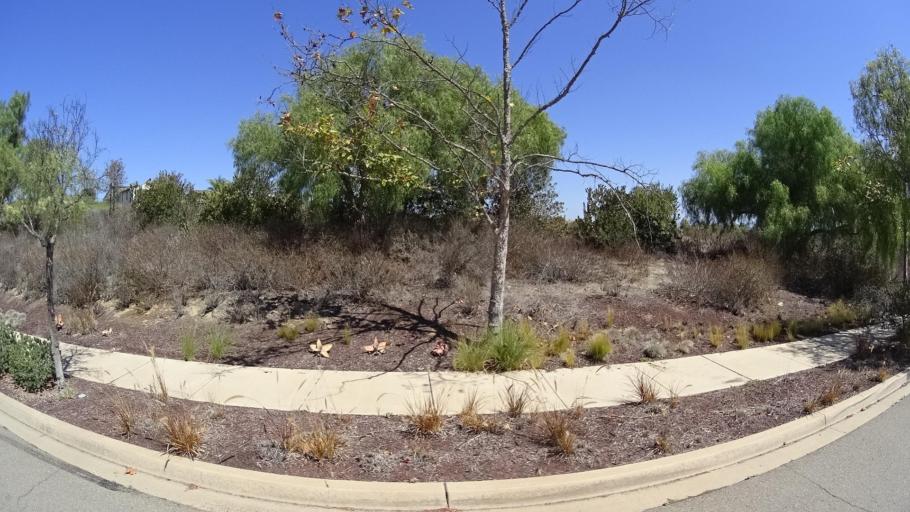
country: US
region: California
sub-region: San Diego County
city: Fairbanks Ranch
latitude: 33.0168
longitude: -117.1504
